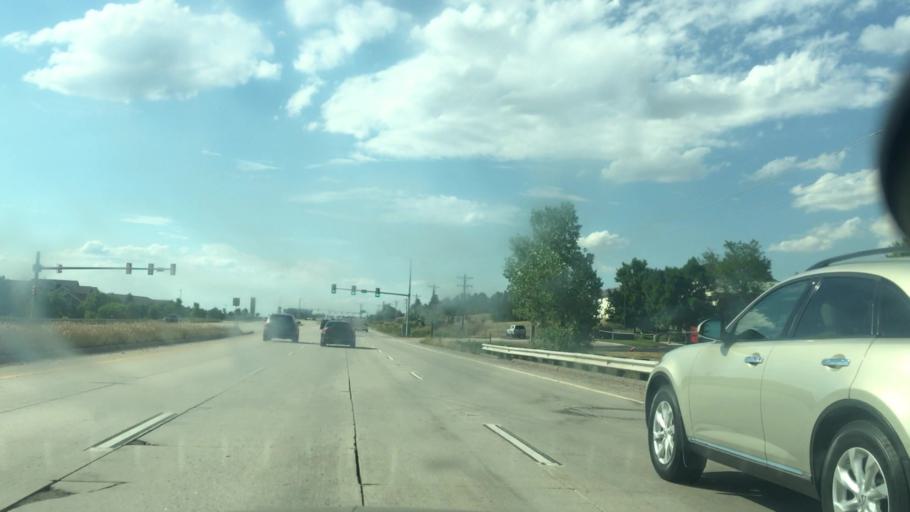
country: US
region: Colorado
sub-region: Arapahoe County
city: Dove Valley
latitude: 39.5836
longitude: -104.7952
